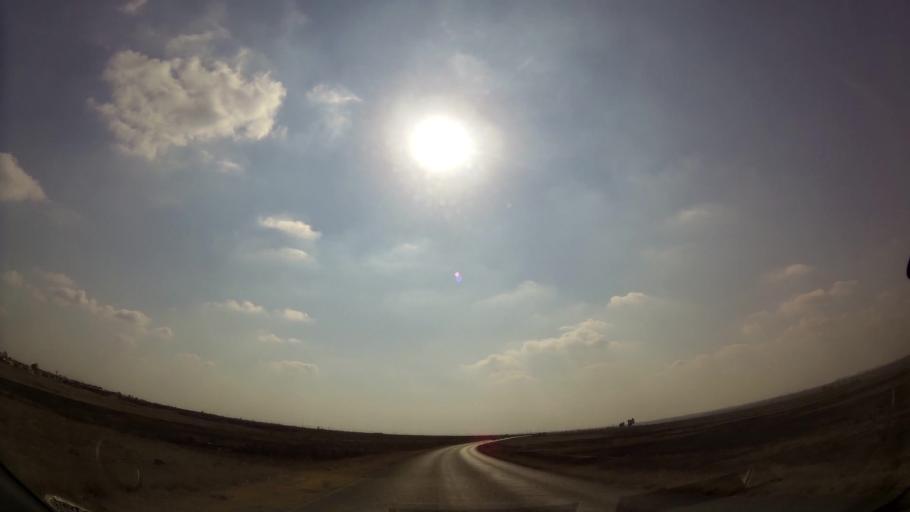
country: ZA
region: Gauteng
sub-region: Ekurhuleni Metropolitan Municipality
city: Springs
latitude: -26.1459
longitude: 28.4450
